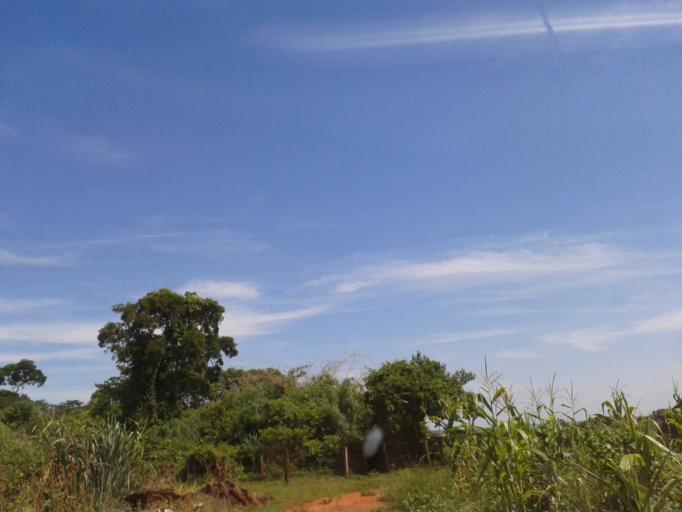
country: BR
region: Minas Gerais
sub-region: Santa Vitoria
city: Santa Vitoria
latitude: -19.1576
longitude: -50.5469
